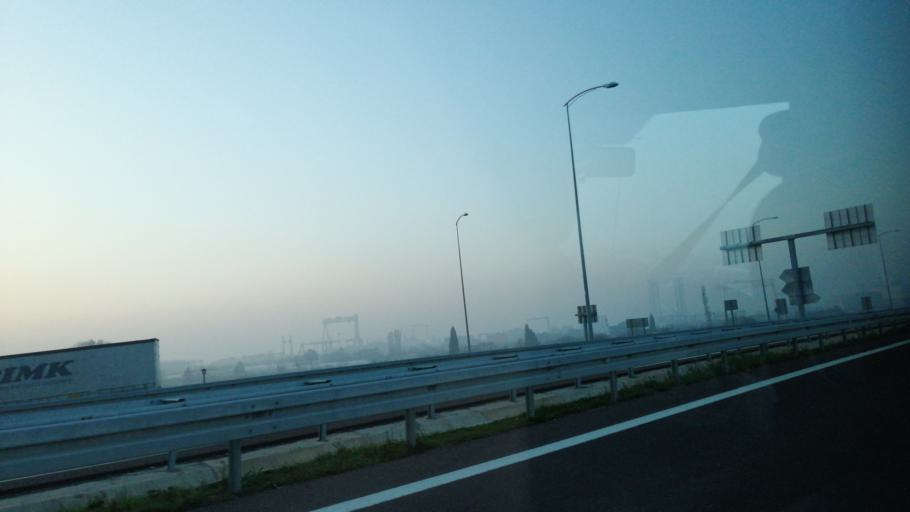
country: TR
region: Yalova
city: Altinova
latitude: 40.6916
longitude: 29.4707
